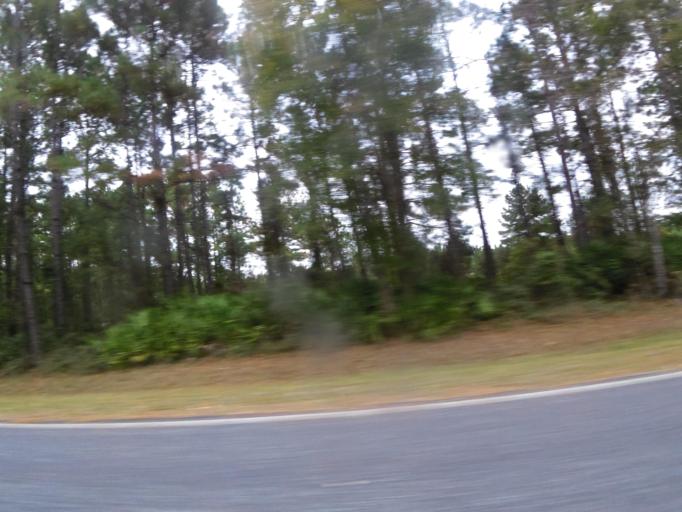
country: US
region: Georgia
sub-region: Charlton County
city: Folkston
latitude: 30.9133
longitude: -82.0825
